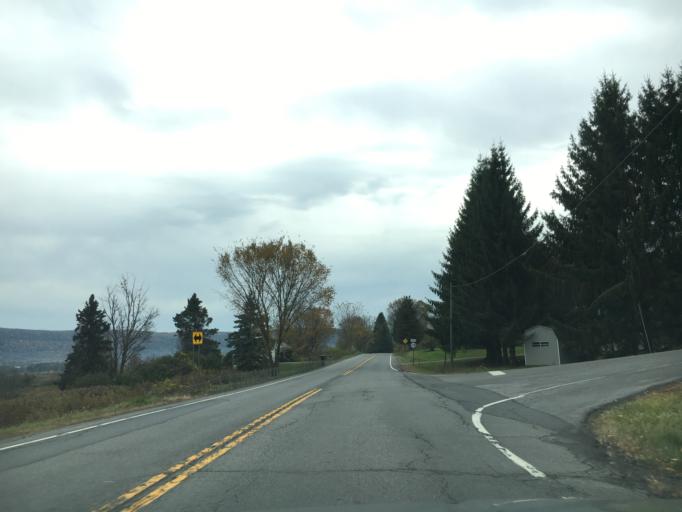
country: US
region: New York
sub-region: Otsego County
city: Cooperstown
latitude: 42.6076
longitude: -74.9564
